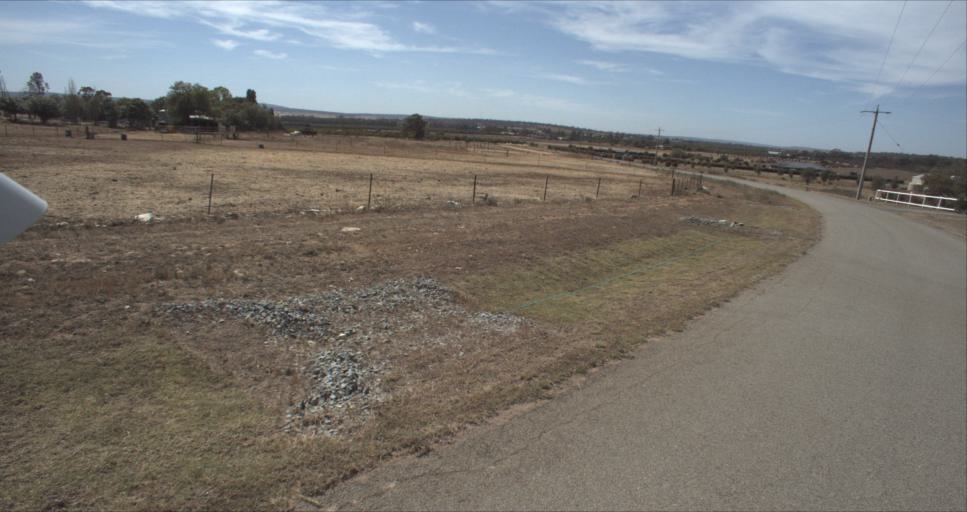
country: AU
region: New South Wales
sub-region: Leeton
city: Leeton
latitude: -34.5769
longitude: 146.4517
